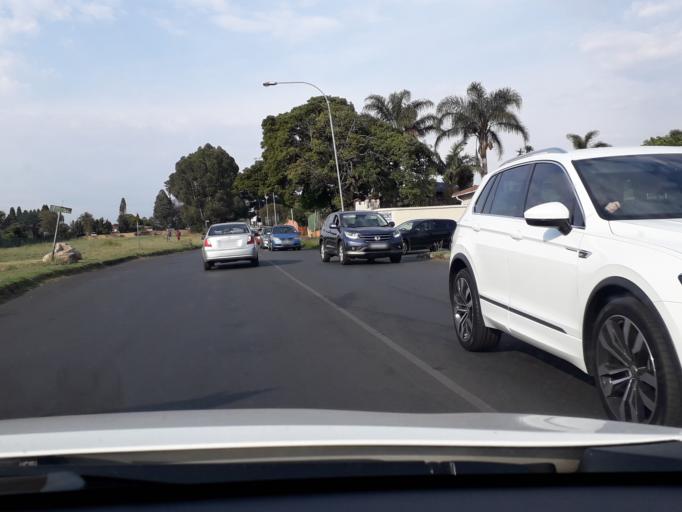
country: ZA
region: Gauteng
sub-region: City of Johannesburg Metropolitan Municipality
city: Johannesburg
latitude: -26.1598
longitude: 27.9775
